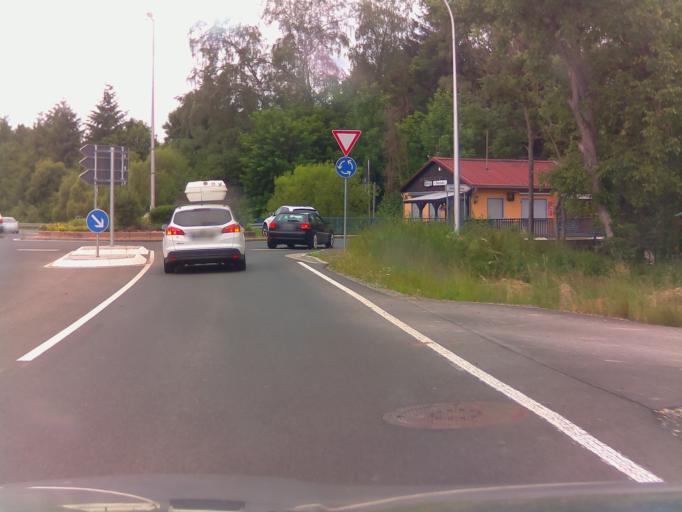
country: DE
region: Bavaria
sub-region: Regierungsbezirk Unterfranken
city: Eschau
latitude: 49.8222
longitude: 9.2559
